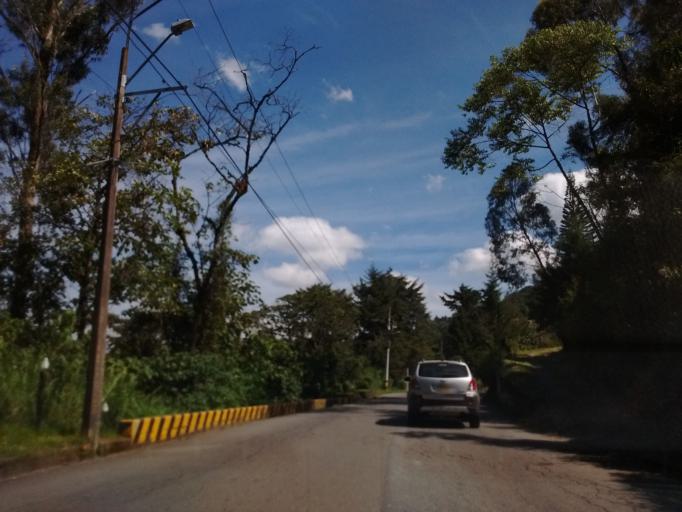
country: CO
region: Antioquia
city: Medellin
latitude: 6.2270
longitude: -75.5144
